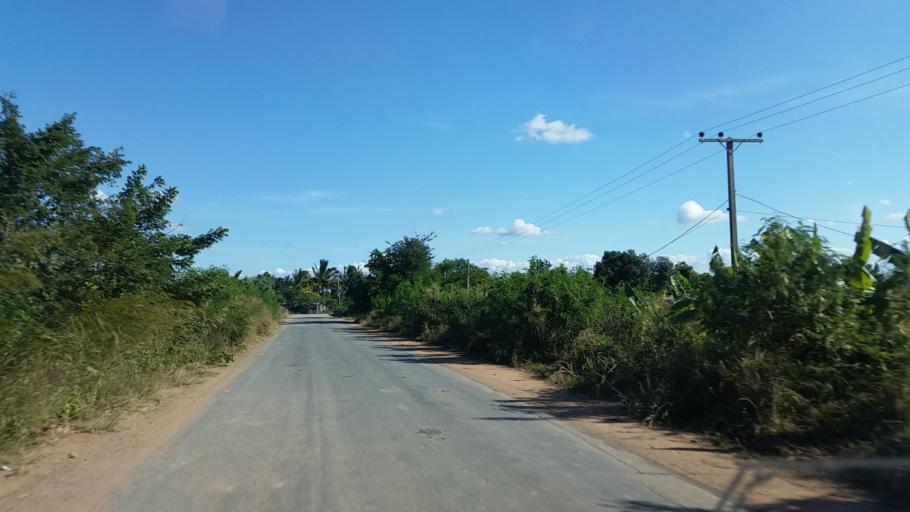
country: TH
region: Chaiyaphum
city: Thep Sathit
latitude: 15.5459
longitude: 101.4747
